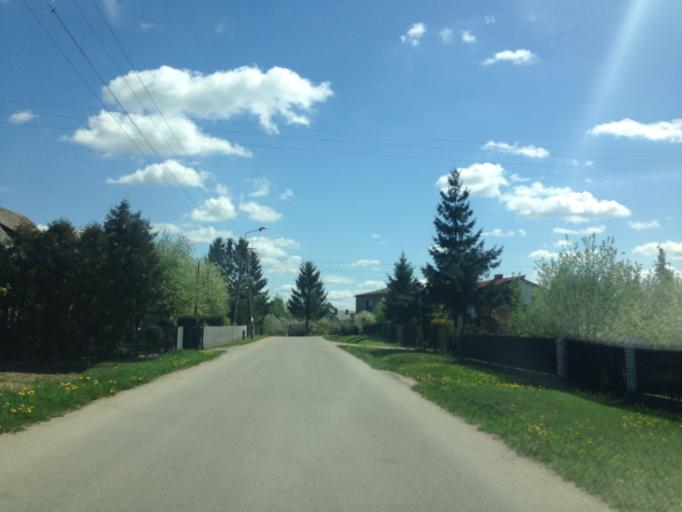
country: PL
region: Kujawsko-Pomorskie
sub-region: Powiat brodnicki
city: Brzozie
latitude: 53.3211
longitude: 19.6078
